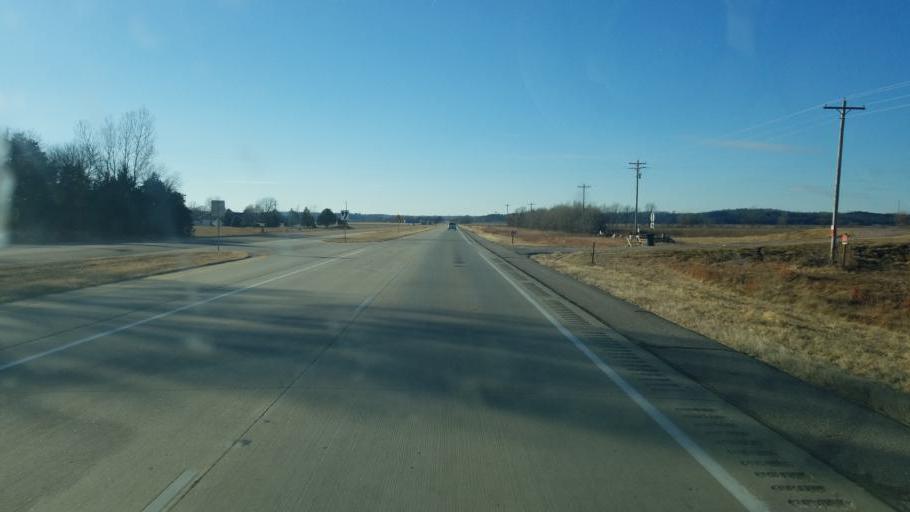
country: US
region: South Dakota
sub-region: Union County
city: Dakota Dunes
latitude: 42.4484
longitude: -96.5287
